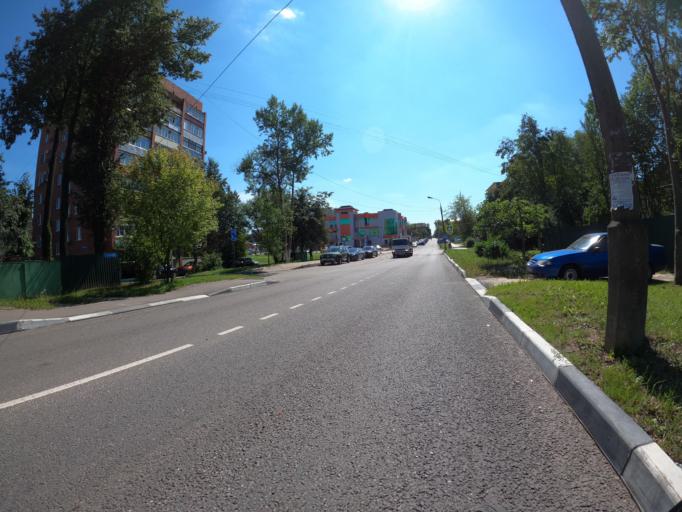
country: RU
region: Moskovskaya
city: Stupino
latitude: 54.8918
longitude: 38.0854
